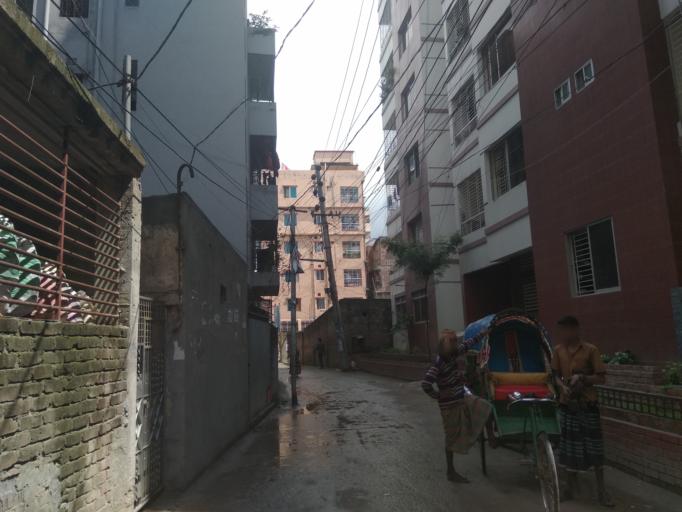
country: BD
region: Dhaka
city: Azimpur
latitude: 23.7977
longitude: 90.3810
